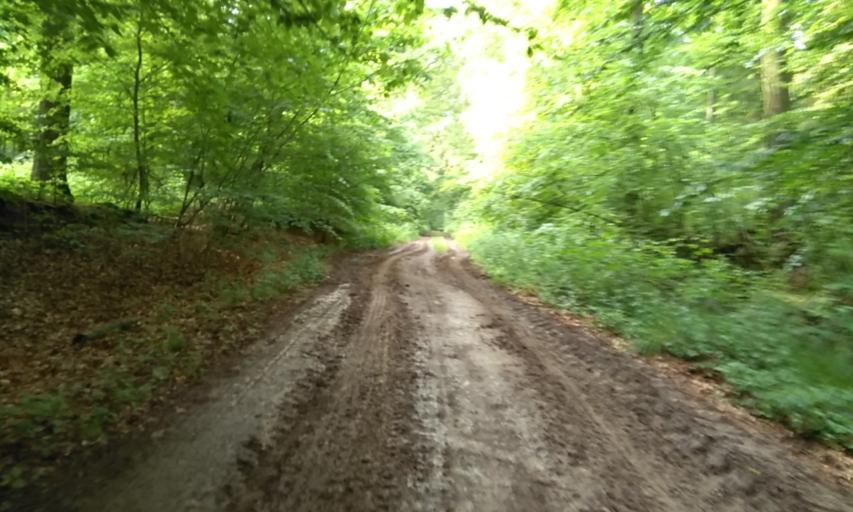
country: DE
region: Lower Saxony
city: Nottensdorf
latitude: 53.4718
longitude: 9.6220
